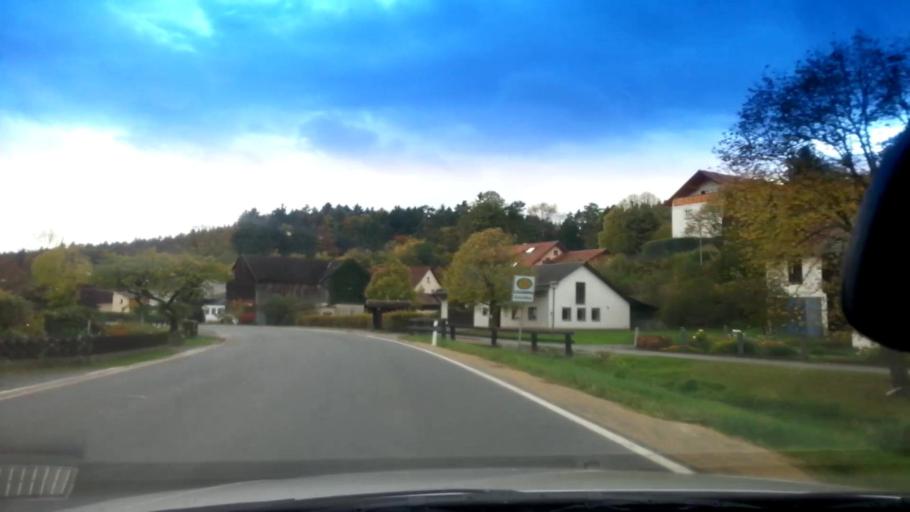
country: DE
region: Bavaria
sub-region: Upper Franconia
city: Wonsees
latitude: 49.9923
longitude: 11.2947
